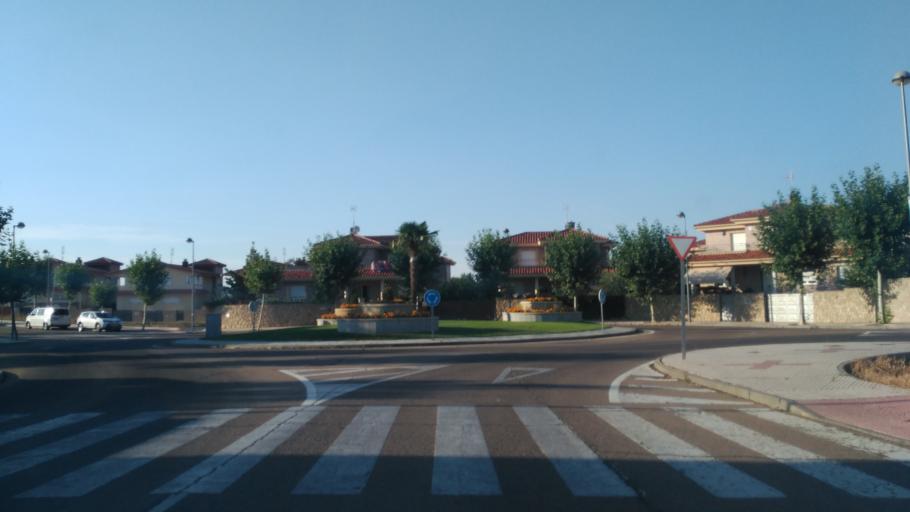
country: ES
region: Castille and Leon
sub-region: Provincia de Salamanca
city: Carbajosa de la Sagrada
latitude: 40.9401
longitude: -5.6452
